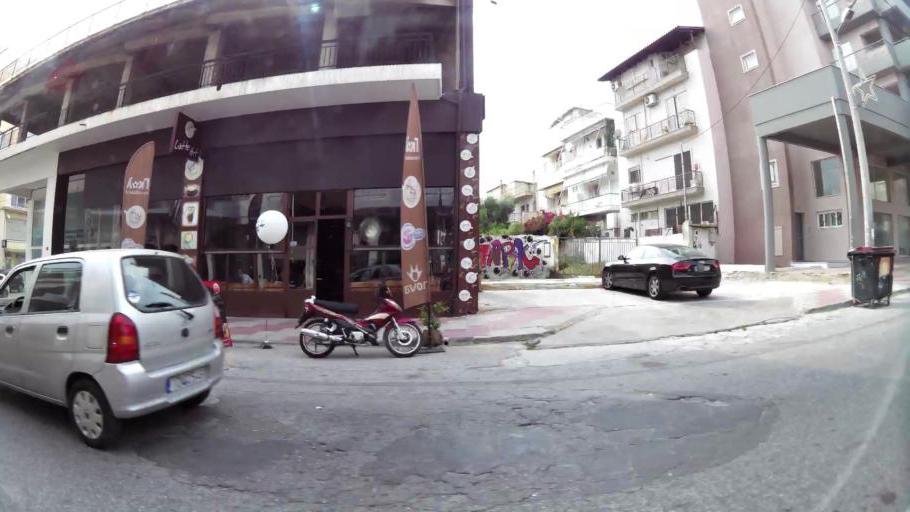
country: GR
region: Attica
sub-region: Nomarchia Athinas
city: Chaidari
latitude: 38.0106
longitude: 23.6786
